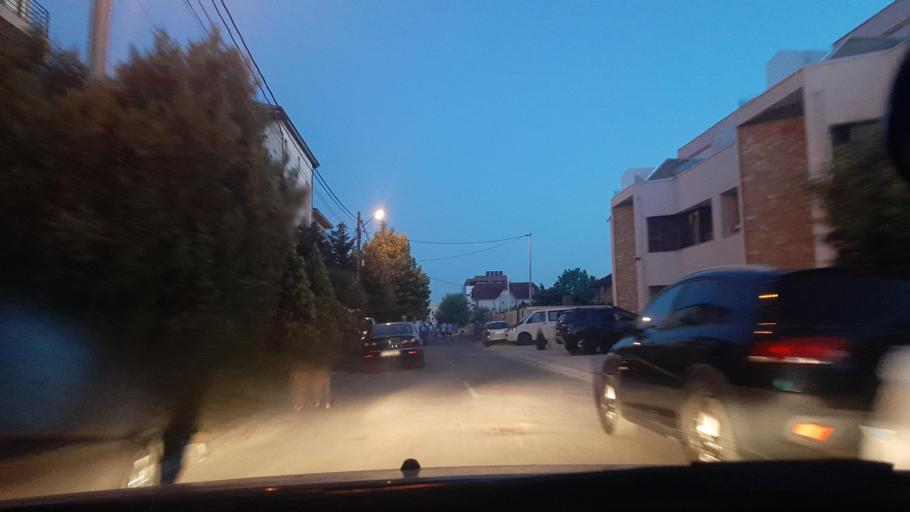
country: RO
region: Constanta
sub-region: Comuna Navodari
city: Navodari
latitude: 44.3025
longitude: 28.6223
